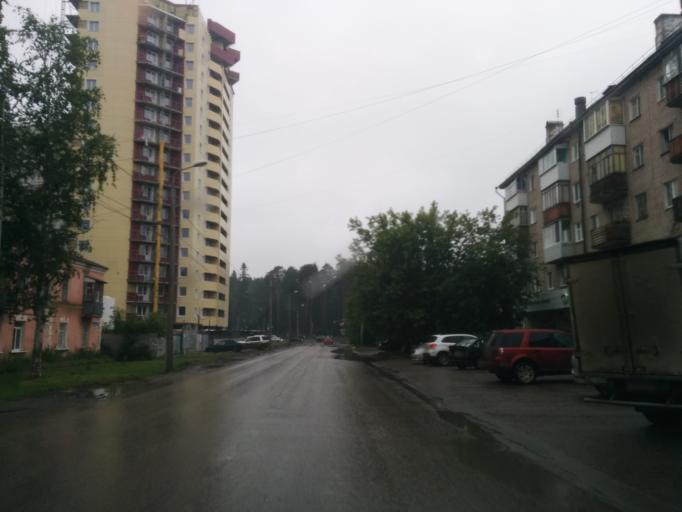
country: RU
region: Perm
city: Kondratovo
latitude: 58.0345
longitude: 56.0239
